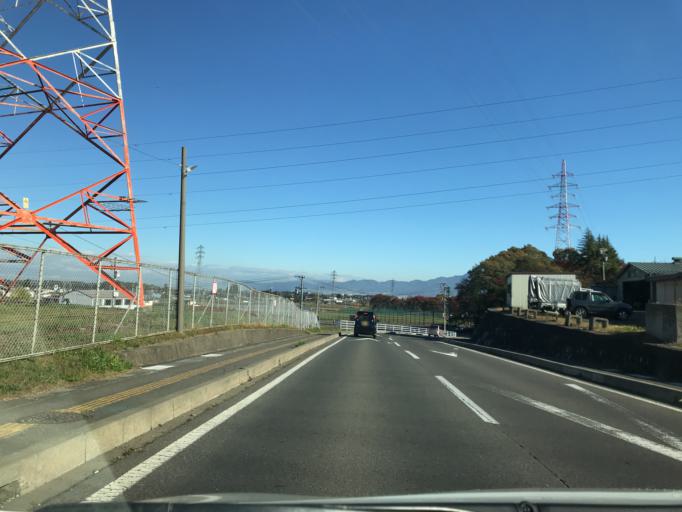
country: JP
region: Nagano
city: Shiojiri
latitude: 36.1255
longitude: 137.9371
